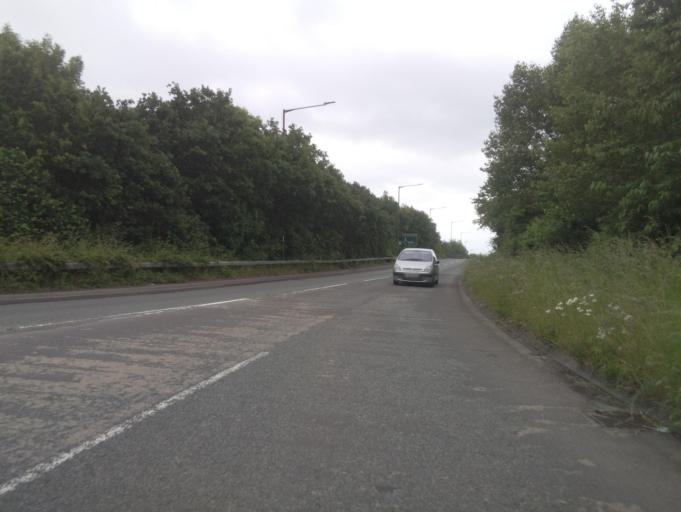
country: GB
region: England
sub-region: Derbyshire
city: Rodsley
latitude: 52.8831
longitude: -1.7025
